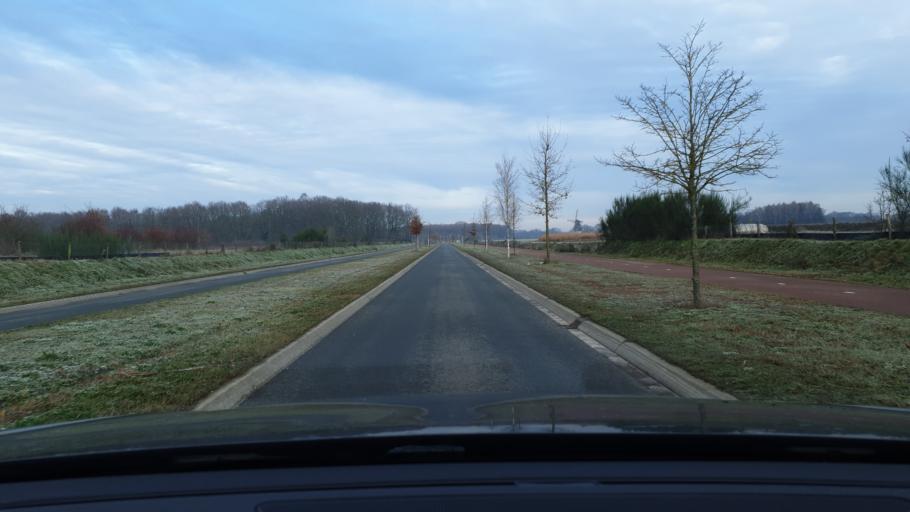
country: NL
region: North Brabant
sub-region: Gemeente Veldhoven
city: Oerle
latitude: 51.4199
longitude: 5.3595
